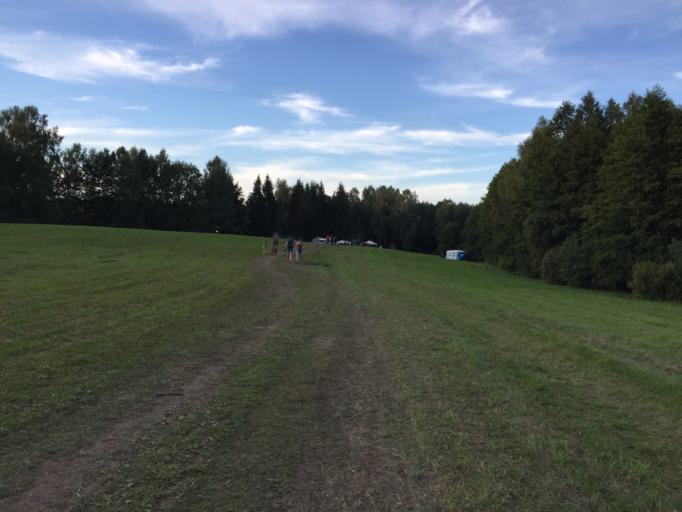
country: LT
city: Zarasai
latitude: 55.7898
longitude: 25.9599
